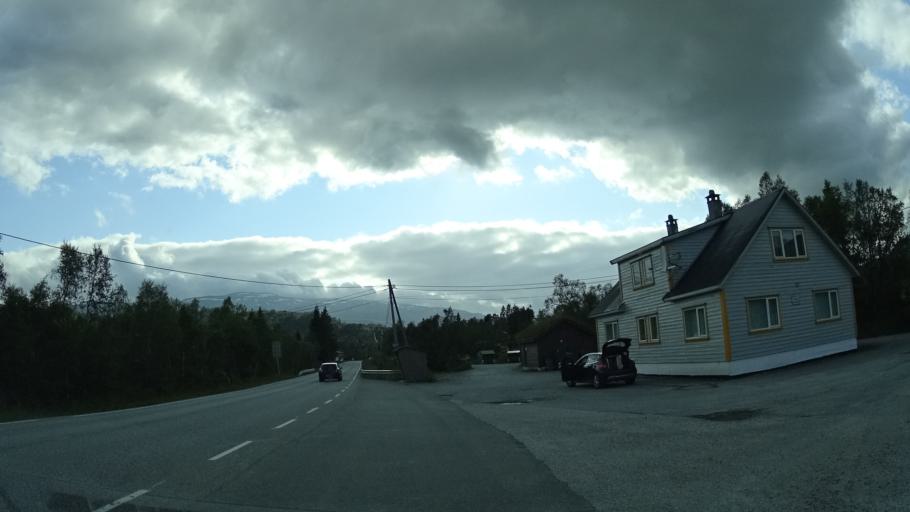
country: NO
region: Hordaland
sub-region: Kvam
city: Norheimsund
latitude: 60.3688
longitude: 6.0281
